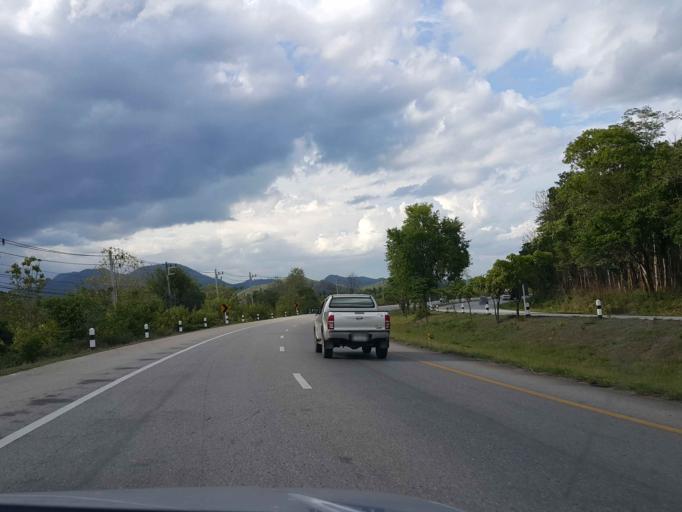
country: TH
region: Lampang
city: Thoen
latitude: 17.7446
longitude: 99.2305
